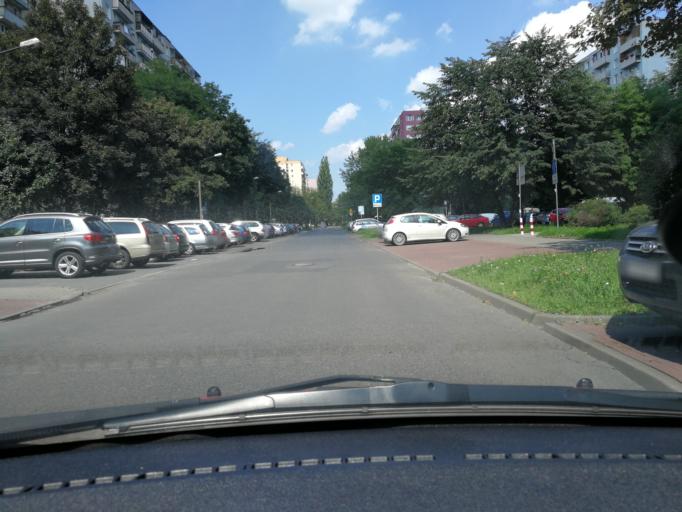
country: PL
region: Masovian Voivodeship
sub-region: Warszawa
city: Targowek
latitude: 52.2874
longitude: 21.0248
